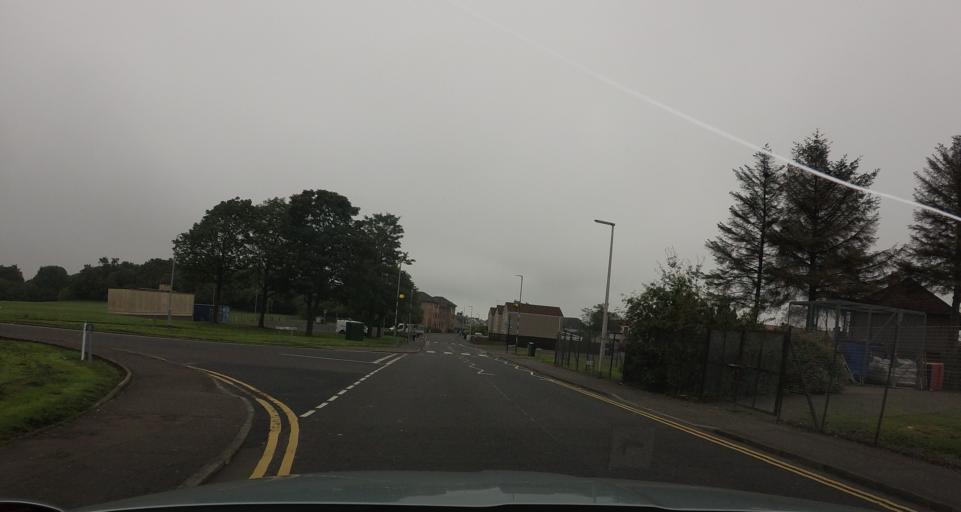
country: GB
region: Scotland
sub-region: Fife
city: Kelty
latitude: 56.1345
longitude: -3.3902
